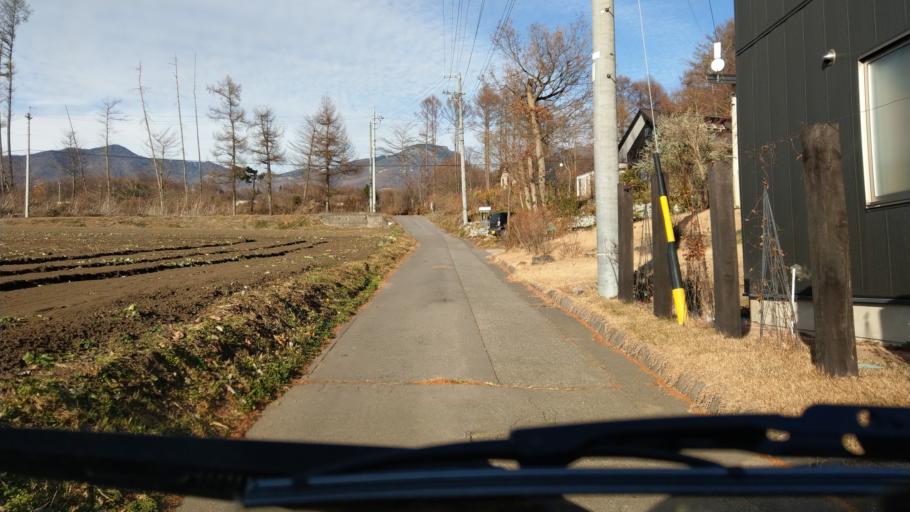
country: JP
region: Nagano
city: Komoro
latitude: 36.3429
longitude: 138.4621
